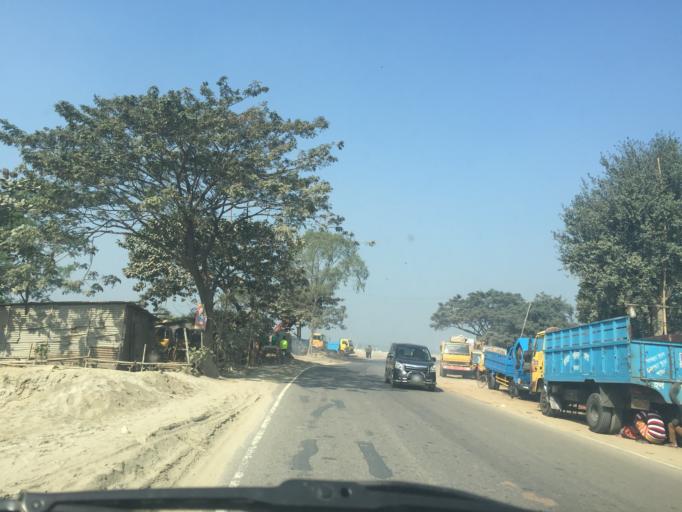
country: BD
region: Dhaka
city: Azimpur
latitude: 23.8076
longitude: 90.3412
